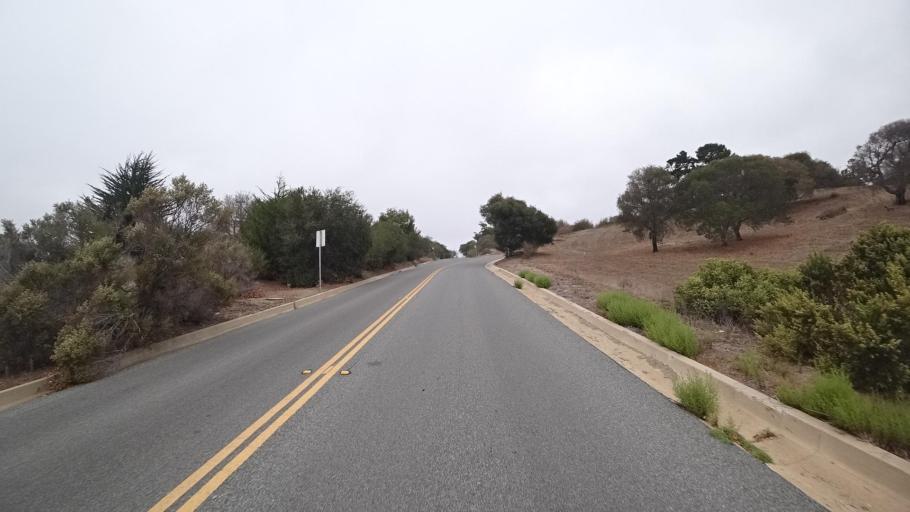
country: US
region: California
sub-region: Monterey County
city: Del Rey Oaks
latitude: 36.5748
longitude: -121.8083
